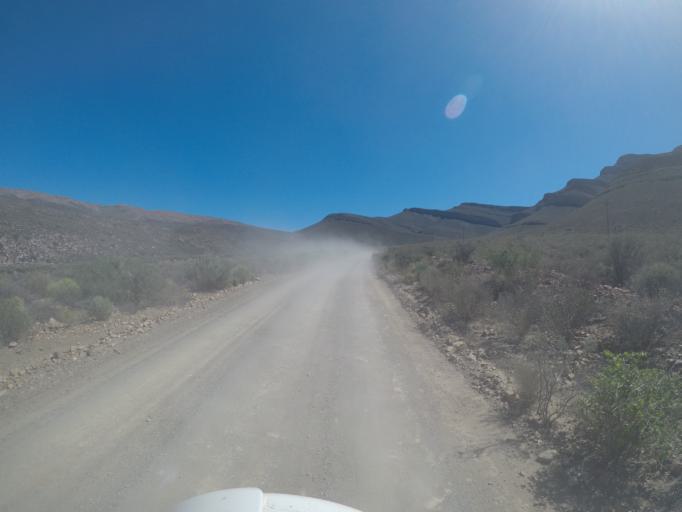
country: ZA
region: Western Cape
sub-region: West Coast District Municipality
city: Clanwilliam
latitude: -32.6275
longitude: 19.3913
